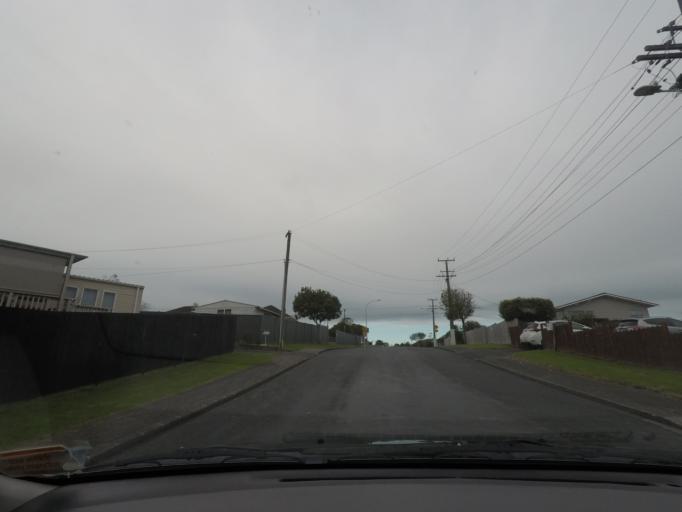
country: NZ
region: Auckland
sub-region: Auckland
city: Rosebank
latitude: -36.8629
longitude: 174.6407
